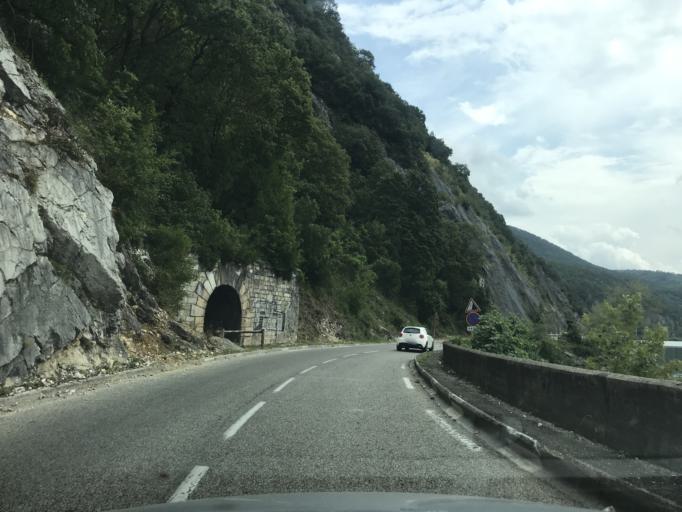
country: FR
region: Rhone-Alpes
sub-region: Departement de la Savoie
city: Brison-Saint-Innocent
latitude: 45.7434
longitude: 5.8881
